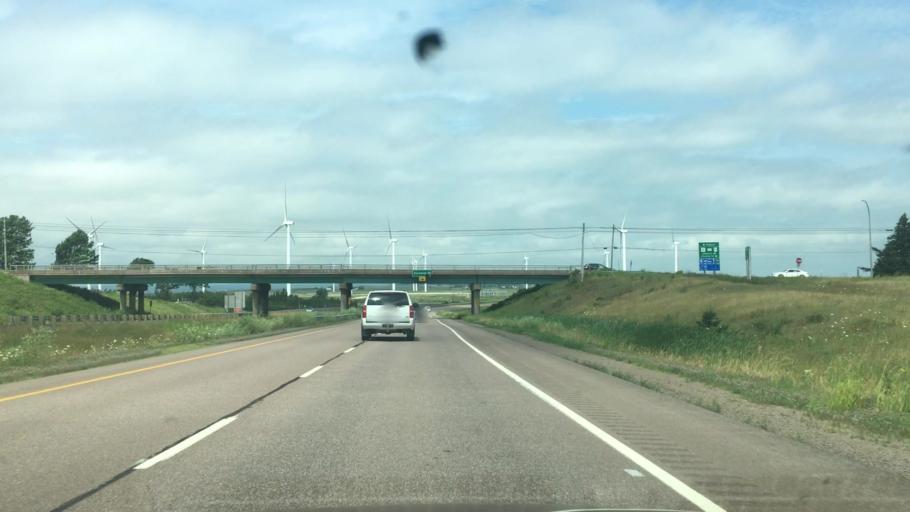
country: CA
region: Nova Scotia
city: Amherst
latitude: 45.8180
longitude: -64.2337
